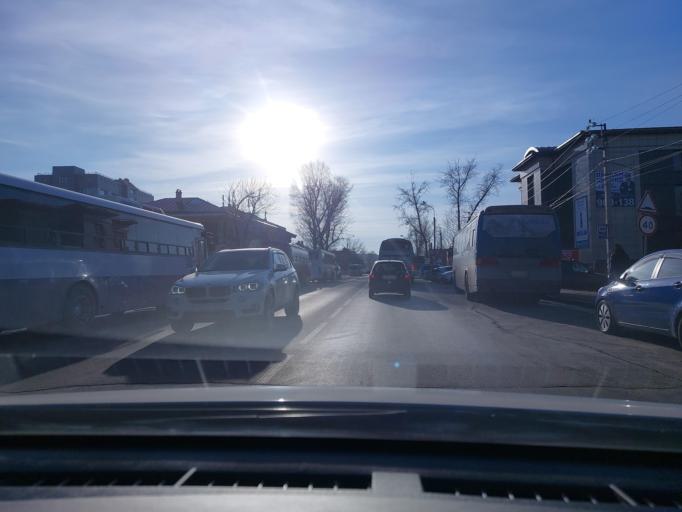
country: RU
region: Irkutsk
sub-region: Irkutskiy Rayon
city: Irkutsk
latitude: 52.2827
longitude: 104.3024
